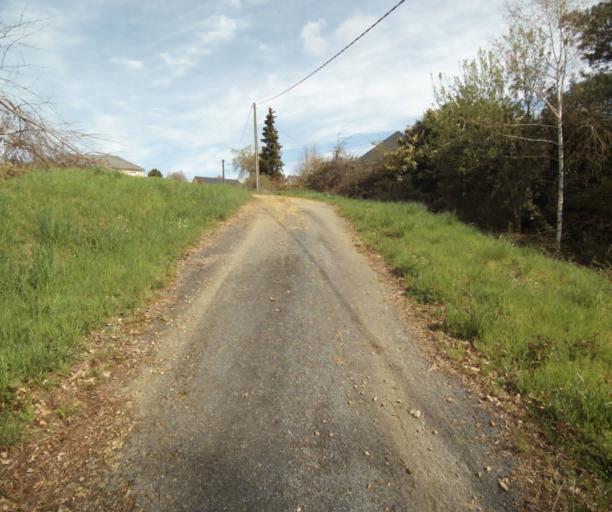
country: FR
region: Limousin
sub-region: Departement de la Correze
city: Laguenne
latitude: 45.2622
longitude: 1.8119
